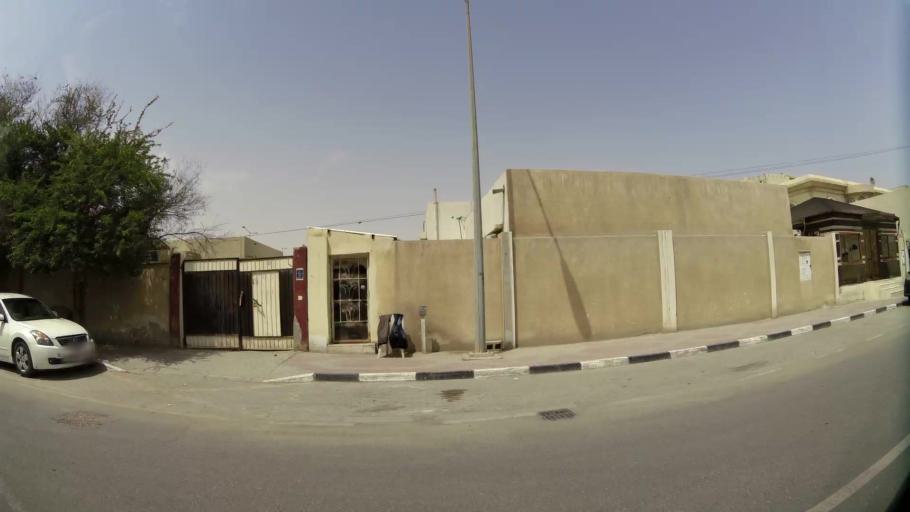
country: QA
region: Baladiyat ar Rayyan
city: Ar Rayyan
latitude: 25.2503
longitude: 51.4291
